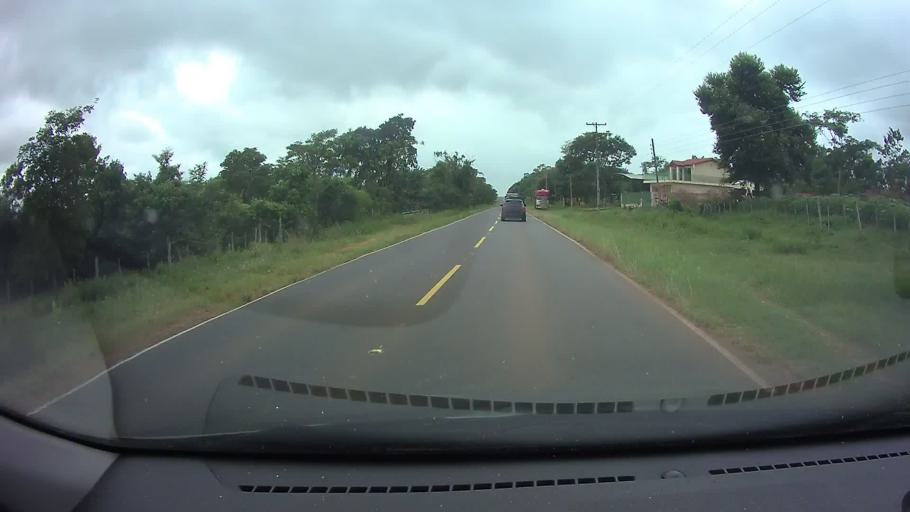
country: PY
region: Paraguari
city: Carapegua
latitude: -25.7426
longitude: -57.2788
